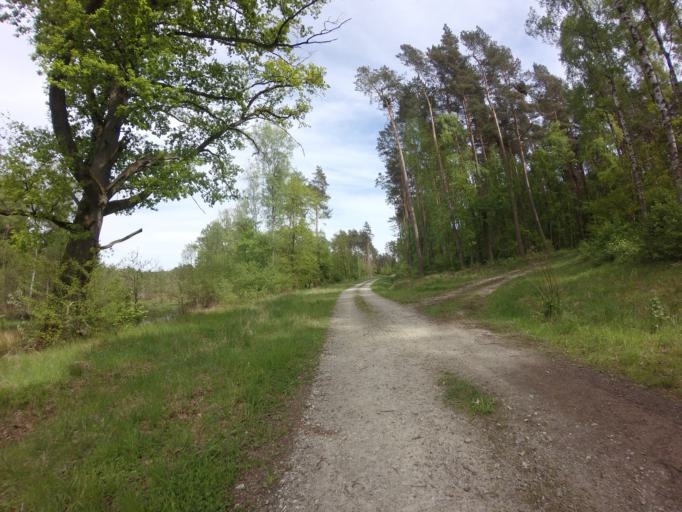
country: PL
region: West Pomeranian Voivodeship
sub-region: Powiat choszczenski
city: Drawno
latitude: 53.1599
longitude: 15.6505
